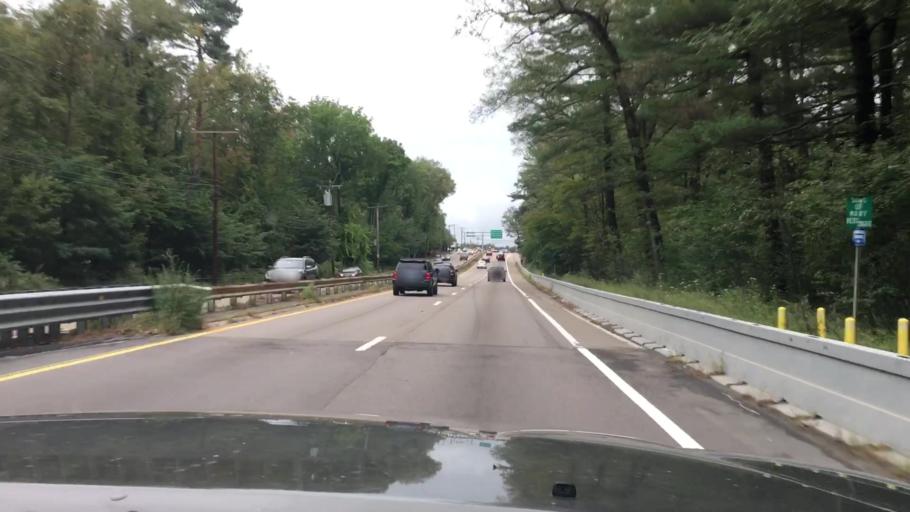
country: US
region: Massachusetts
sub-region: Middlesex County
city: Framingham Center
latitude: 42.2955
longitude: -71.4549
